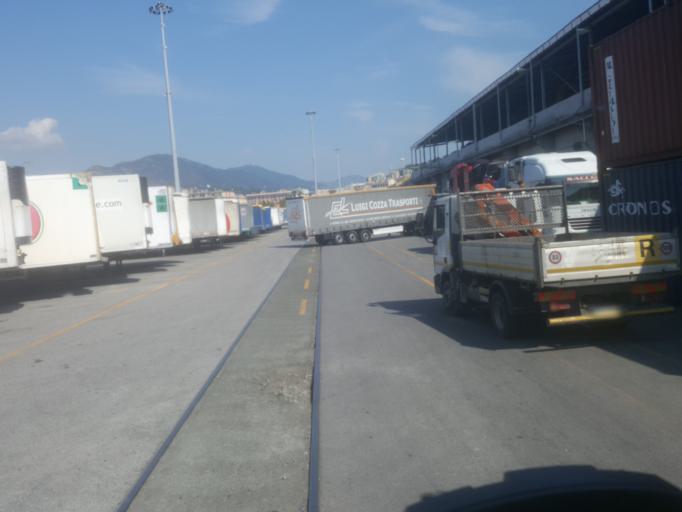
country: IT
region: Liguria
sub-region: Provincia di Genova
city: San Teodoro
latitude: 44.4053
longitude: 8.8901
